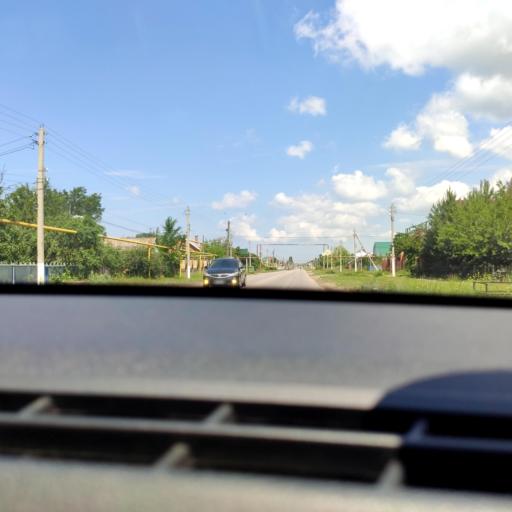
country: RU
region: Samara
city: Podstepki
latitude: 53.6104
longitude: 49.0436
